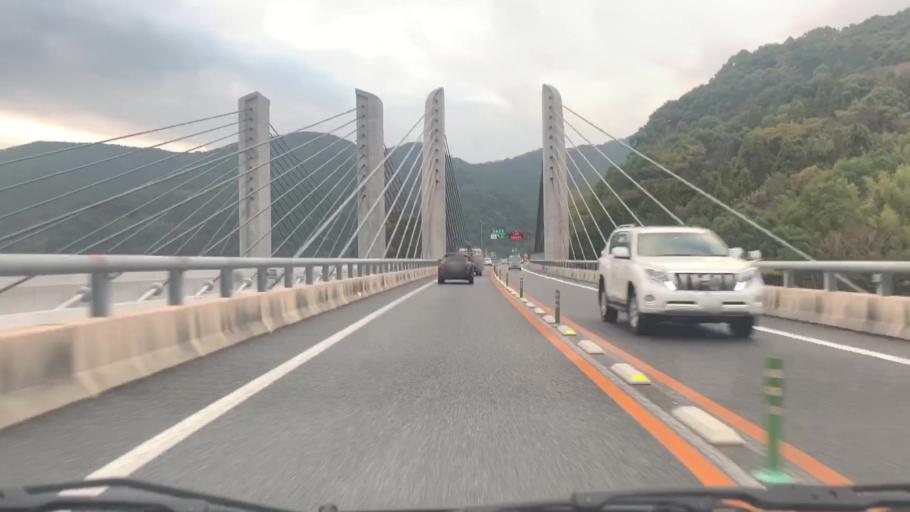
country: JP
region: Nagasaki
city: Nagasaki-shi
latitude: 32.7575
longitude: 129.9289
